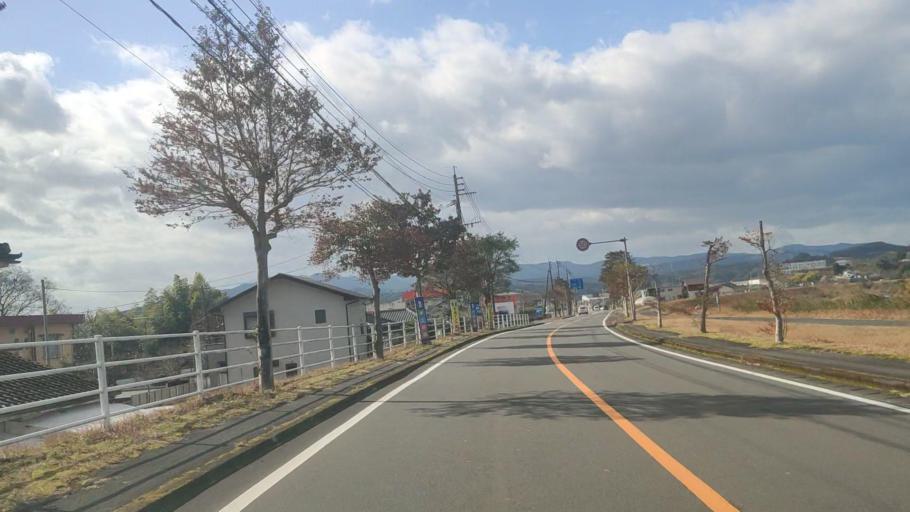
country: JP
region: Kagoshima
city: Okuchi-shinohara
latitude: 31.9545
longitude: 130.7242
